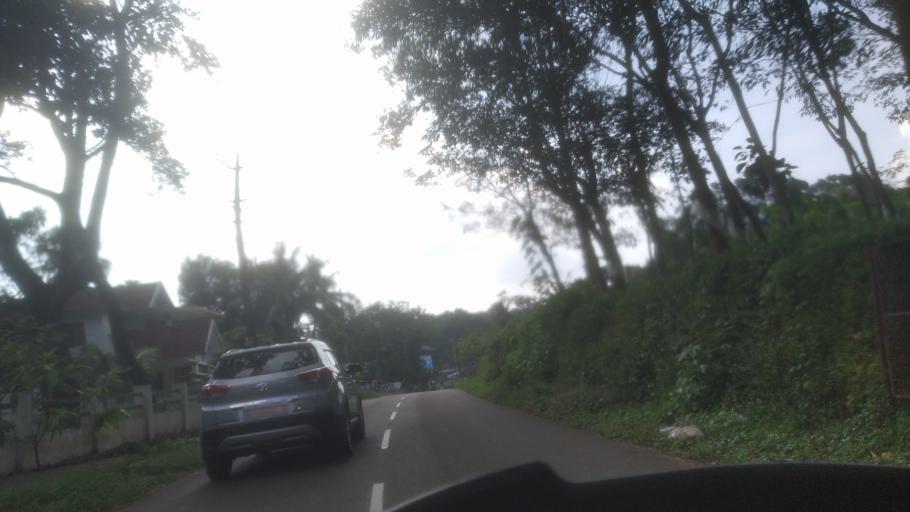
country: IN
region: Kerala
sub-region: Ernakulam
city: Kotamangalam
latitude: 10.0005
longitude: 76.6477
